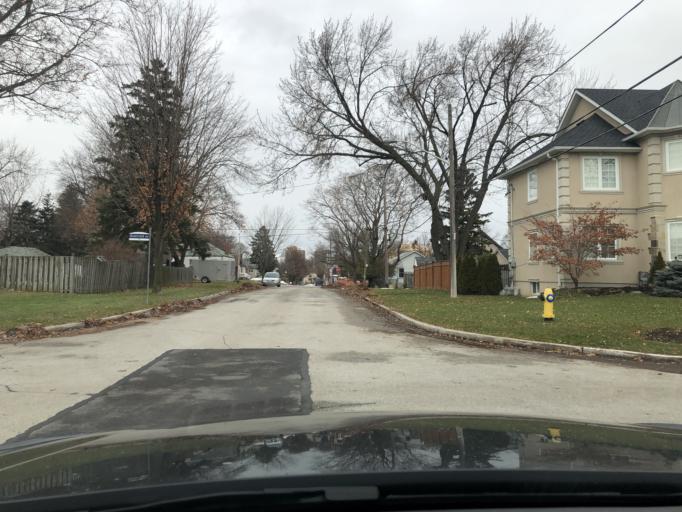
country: CA
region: Ontario
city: Etobicoke
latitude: 43.6959
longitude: -79.5291
